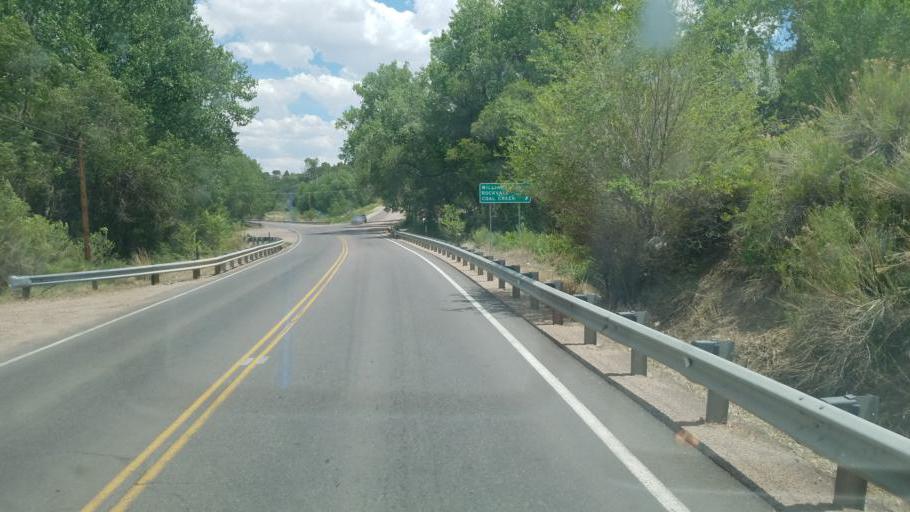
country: US
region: Colorado
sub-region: Fremont County
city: Florence
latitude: 38.4063
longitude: -105.1663
